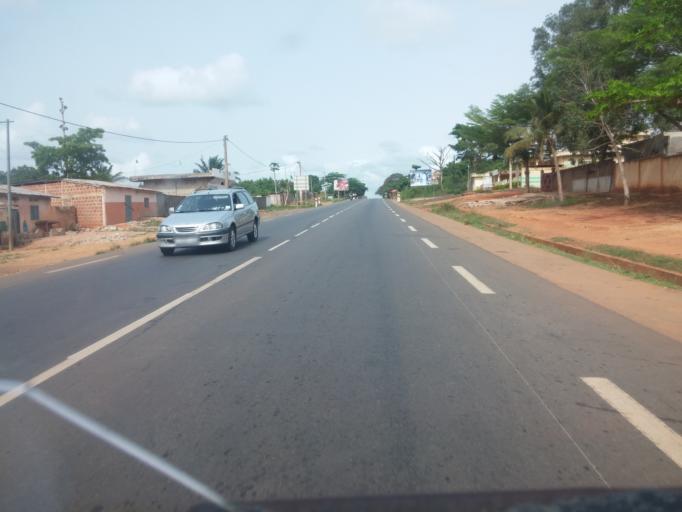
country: BJ
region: Mono
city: Come
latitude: 6.4001
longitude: 1.8891
